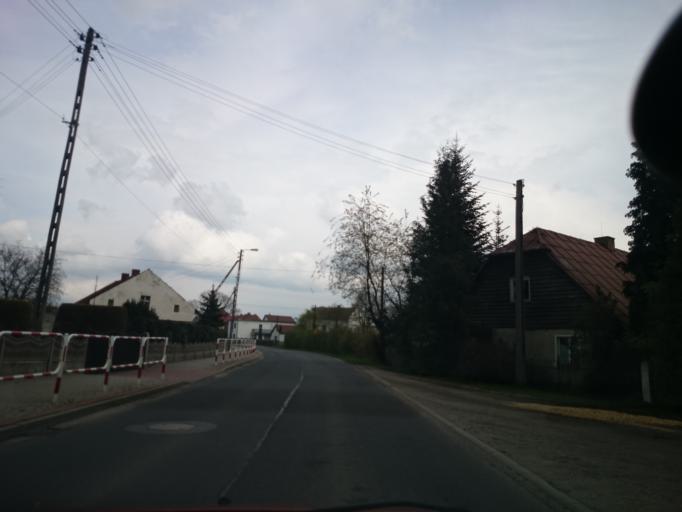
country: PL
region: Opole Voivodeship
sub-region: Powiat strzelecki
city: Izbicko
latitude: 50.5543
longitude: 18.1459
